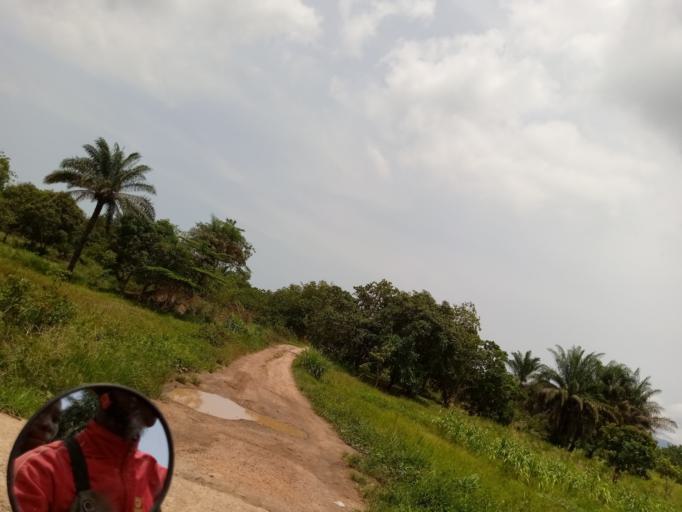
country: SL
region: Western Area
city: Waterloo
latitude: 8.3193
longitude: -13.0346
